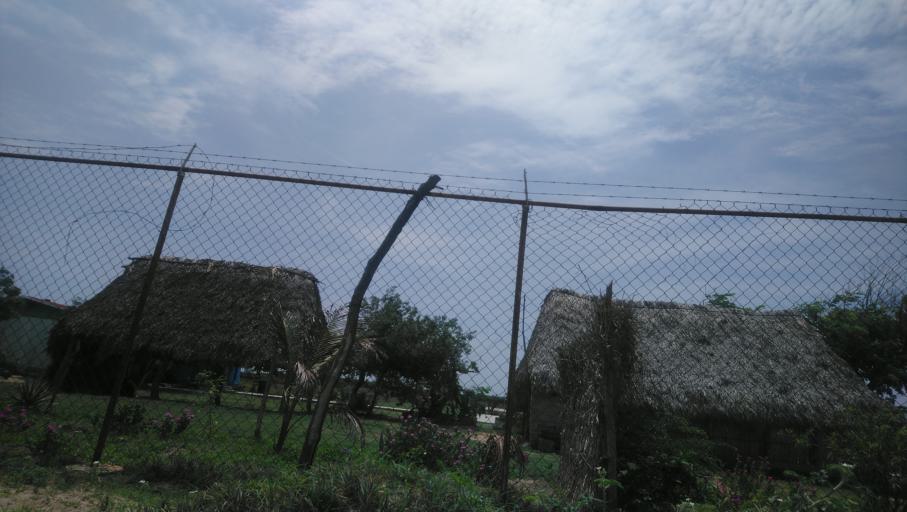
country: MX
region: Oaxaca
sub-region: San Mateo del Mar
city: Colonia Juarez
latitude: 16.2135
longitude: -95.0357
